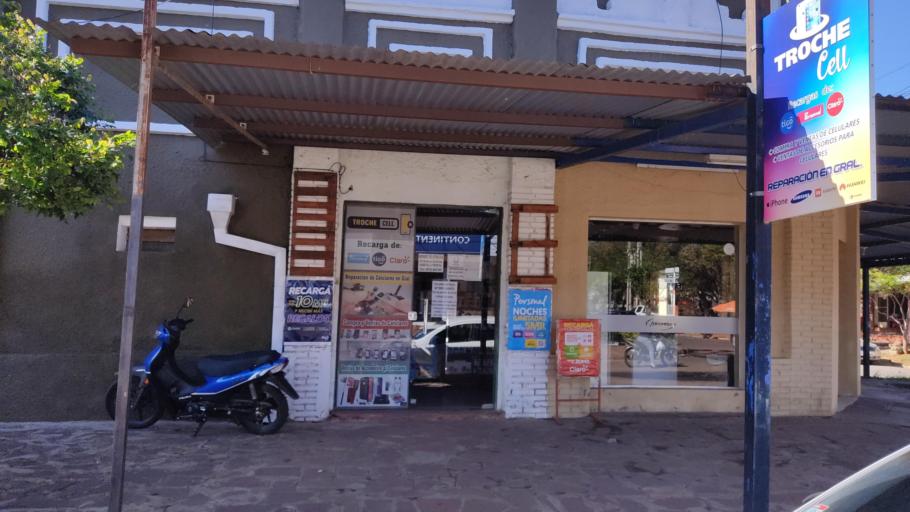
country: PY
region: Misiones
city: San Juan Bautista
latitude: -26.6696
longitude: -57.1391
